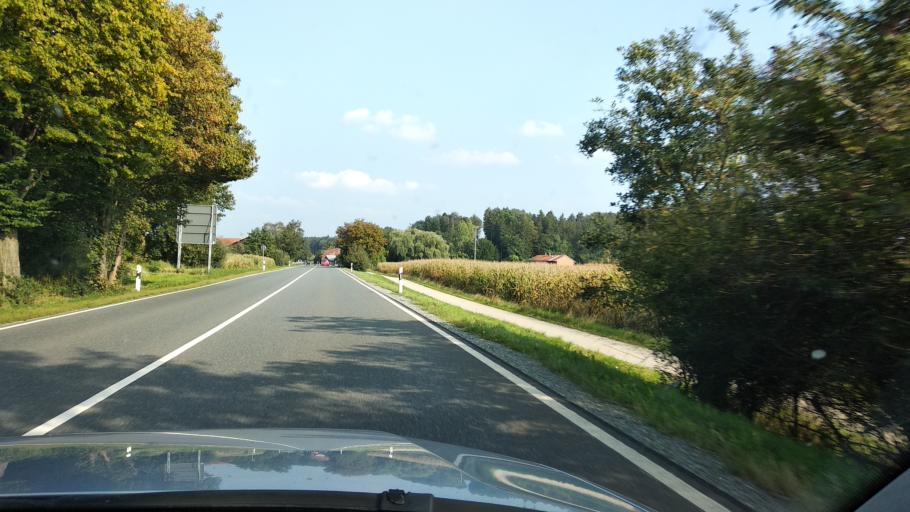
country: DE
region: Bavaria
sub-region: Upper Bavaria
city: Steinhoring
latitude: 48.0844
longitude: 12.0382
